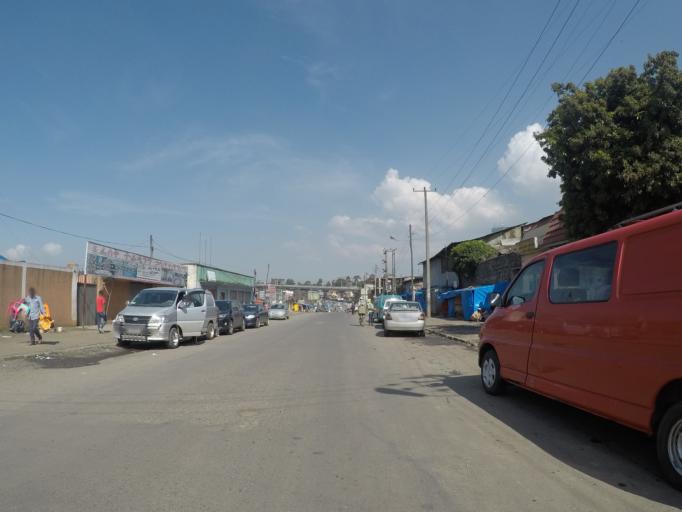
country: ET
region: Adis Abeba
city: Addis Ababa
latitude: 9.0329
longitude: 38.7457
